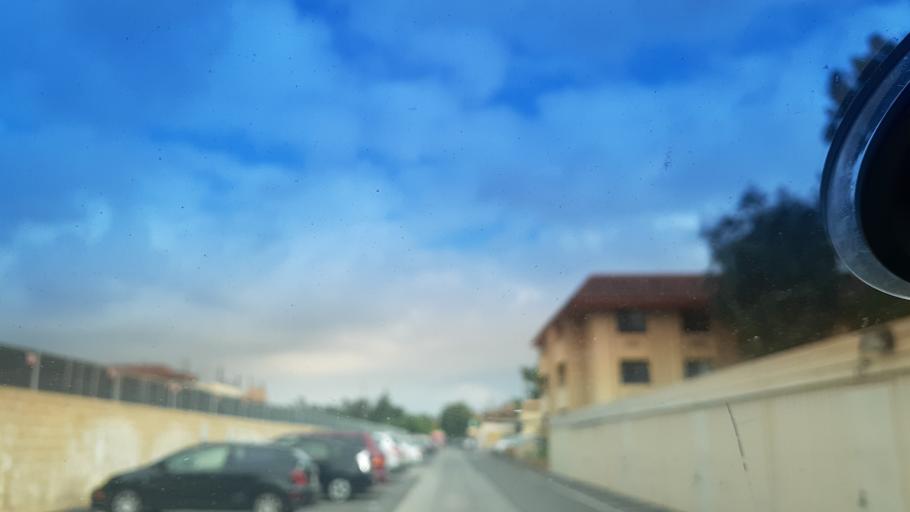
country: US
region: California
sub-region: Orange County
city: Orange
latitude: 33.7750
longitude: -117.8630
